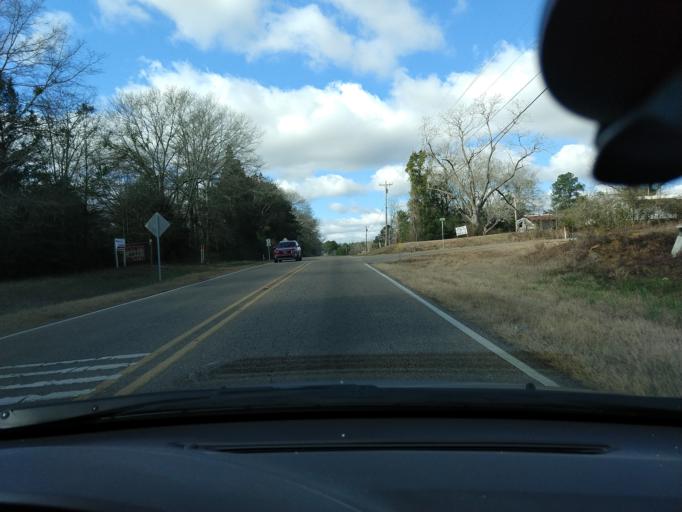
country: US
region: Alabama
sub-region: Coffee County
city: Enterprise
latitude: 31.3241
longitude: -85.8923
